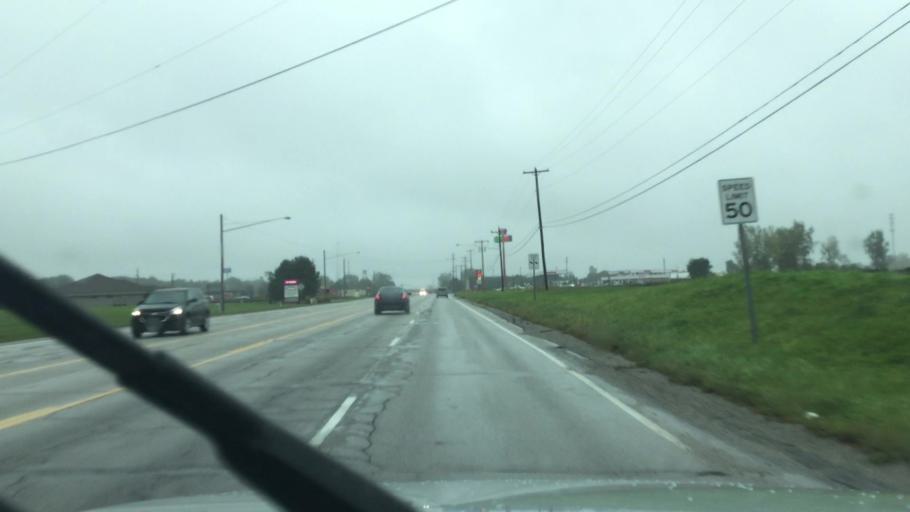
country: US
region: Michigan
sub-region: Saginaw County
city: Bridgeport
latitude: 43.3466
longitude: -83.8560
